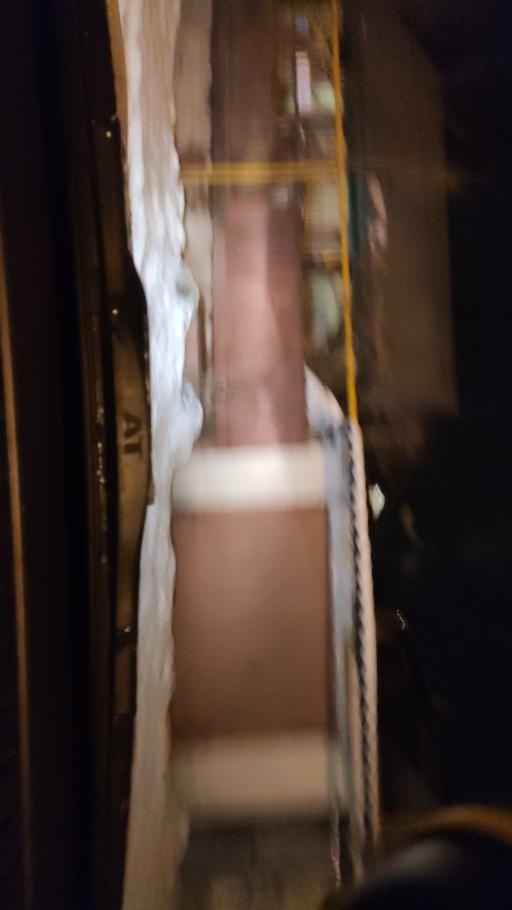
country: RU
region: Samara
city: Zhigulevsk
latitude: 53.4712
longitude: 49.6153
